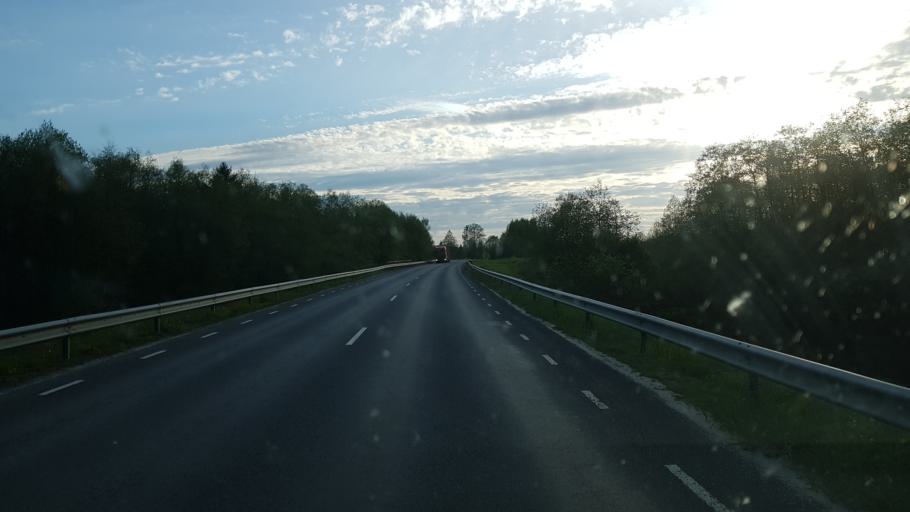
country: EE
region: Jaervamaa
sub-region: Tueri vald
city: Sarevere
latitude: 58.7997
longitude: 25.2498
